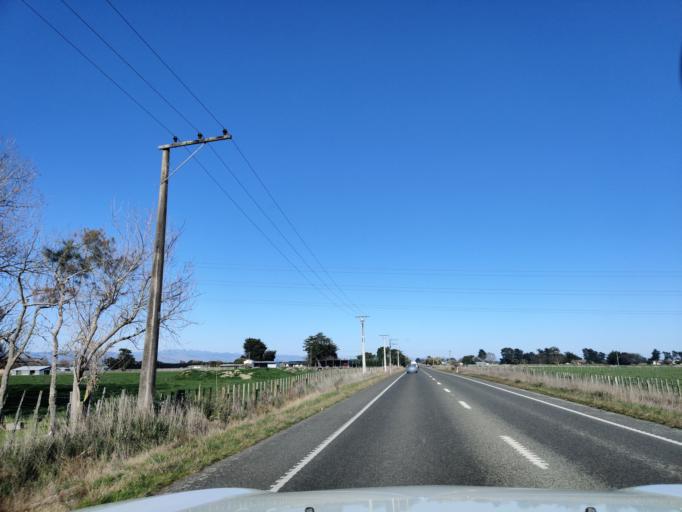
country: NZ
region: Manawatu-Wanganui
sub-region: Palmerston North City
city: Palmerston North
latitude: -40.2558
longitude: 175.5756
